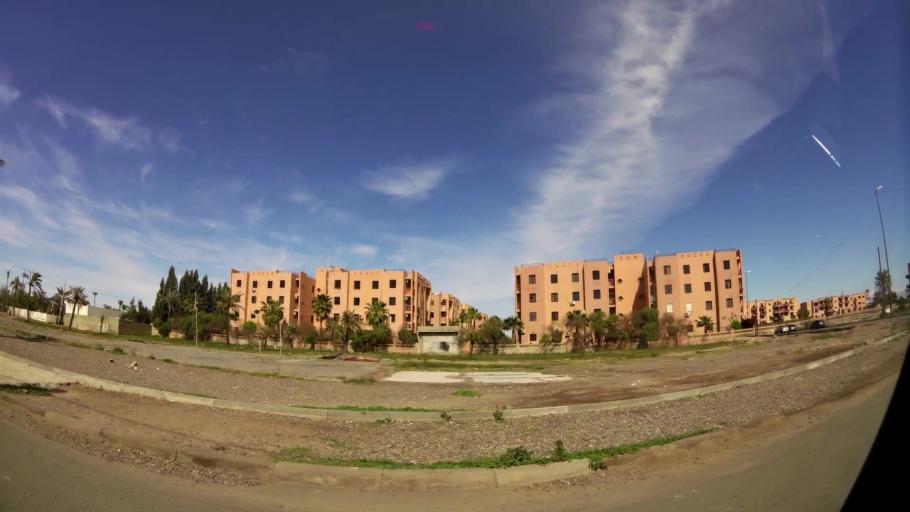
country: MA
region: Marrakech-Tensift-Al Haouz
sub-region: Marrakech
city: Marrakesh
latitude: 31.6441
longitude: -7.9776
